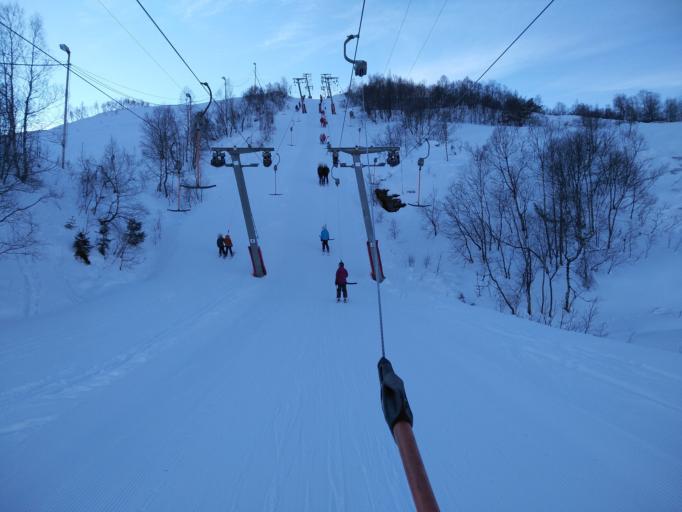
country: NO
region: Rogaland
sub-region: Sauda
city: Sauda
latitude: 59.6207
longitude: 6.2375
